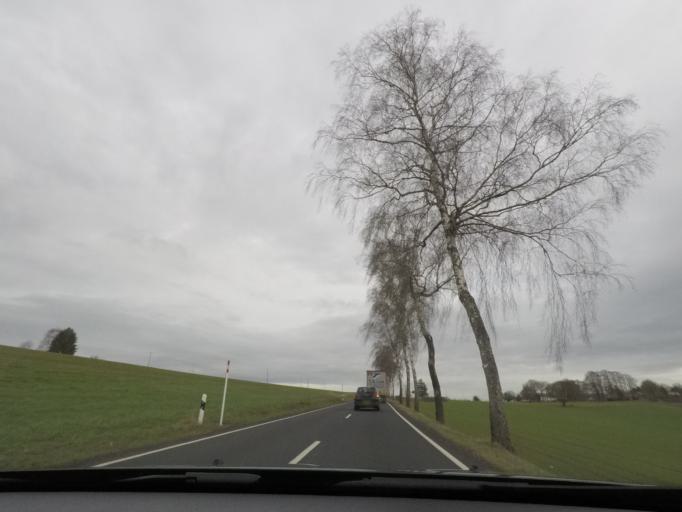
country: LU
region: Diekirch
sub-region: Canton de Wiltz
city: Winseler
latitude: 50.0100
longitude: 5.8732
